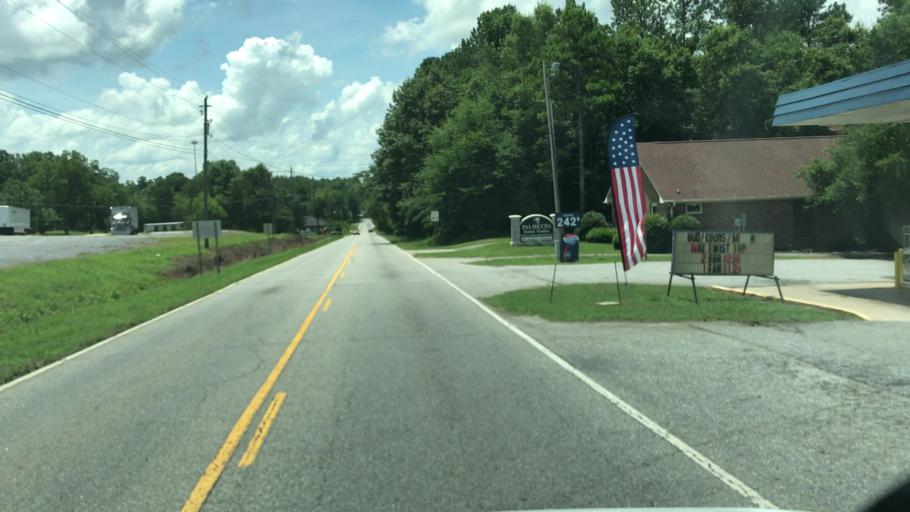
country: US
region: South Carolina
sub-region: Anderson County
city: Williamston
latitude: 34.6415
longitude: -82.4665
